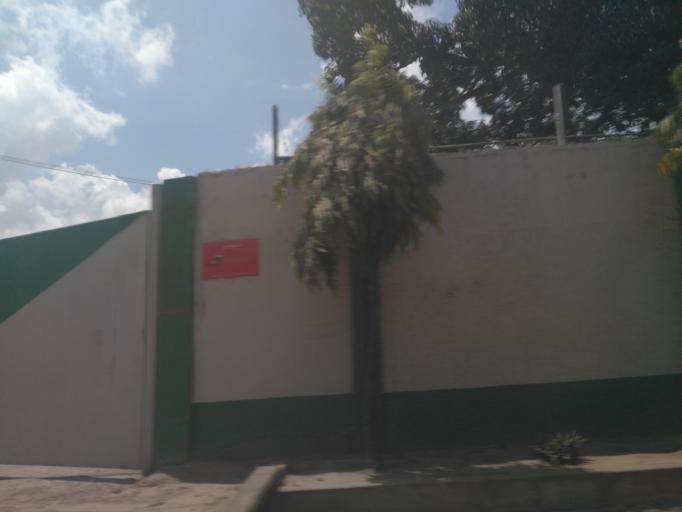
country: TZ
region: Dar es Salaam
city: Dar es Salaam
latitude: -6.8426
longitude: 39.2603
